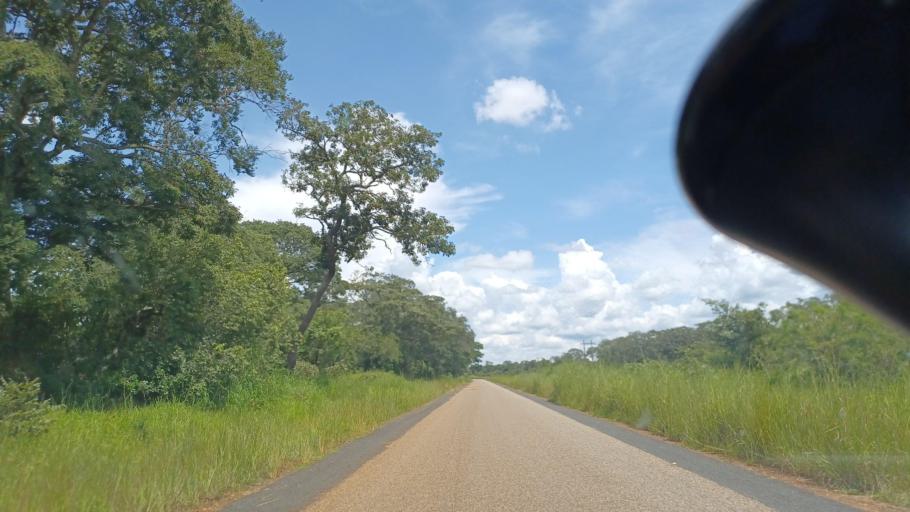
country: ZM
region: North-Western
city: Solwezi
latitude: -12.5761
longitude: 26.1328
